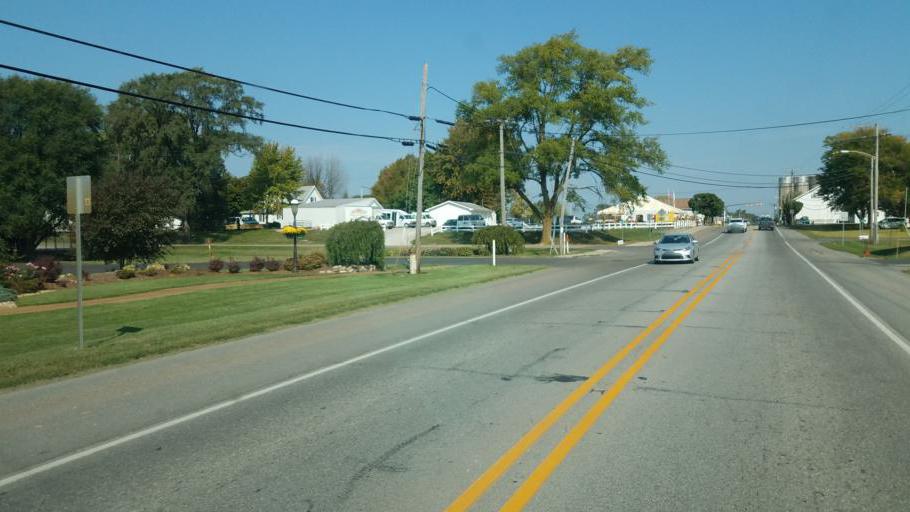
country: US
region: Indiana
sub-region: Elkhart County
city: Middlebury
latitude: 41.6745
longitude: -85.5806
